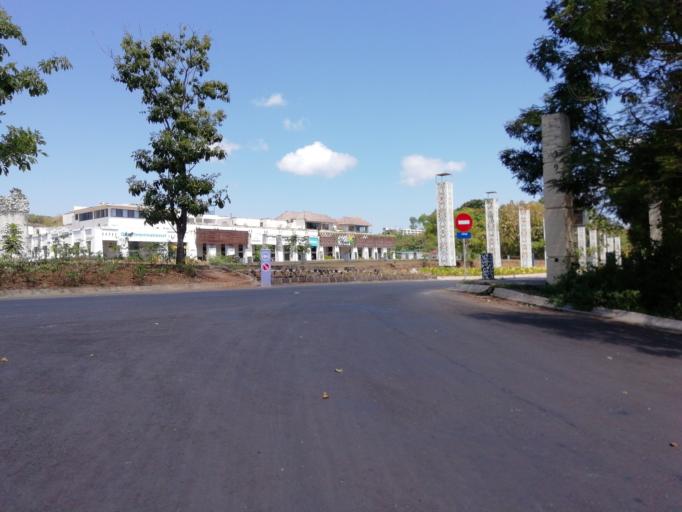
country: ID
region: Bali
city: Jimbaran
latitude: -8.8069
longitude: 115.1644
